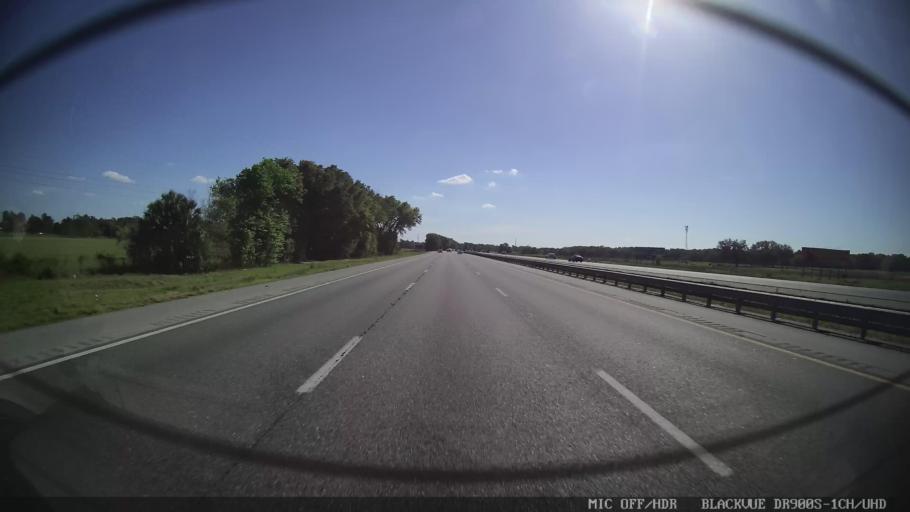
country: US
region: Florida
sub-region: Sumter County
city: Bushnell
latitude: 28.6383
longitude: -82.1627
